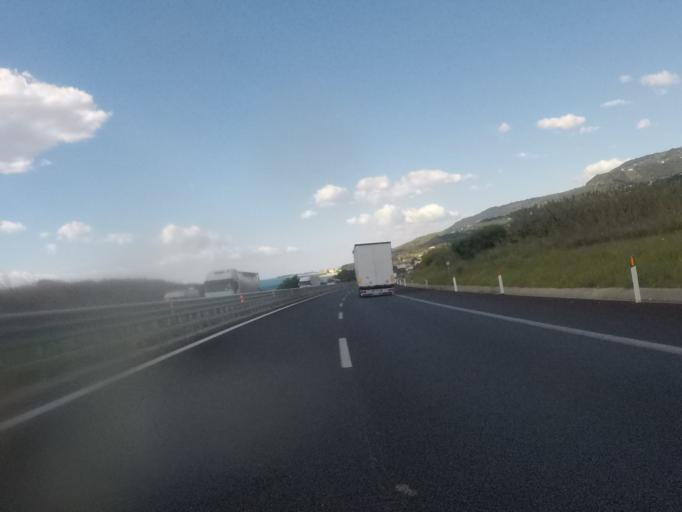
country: IT
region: Calabria
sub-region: Provincia di Catanzaro
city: Falerna Scalo
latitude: 38.9550
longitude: 16.1571
